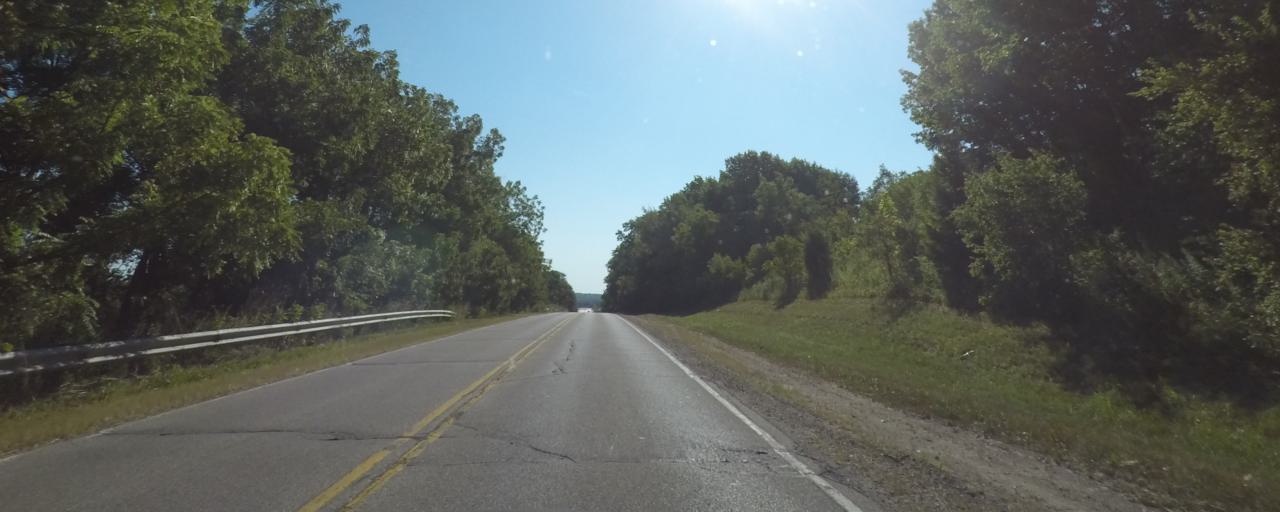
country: US
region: Wisconsin
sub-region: Waukesha County
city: Waukesha
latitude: 42.9885
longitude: -88.2938
